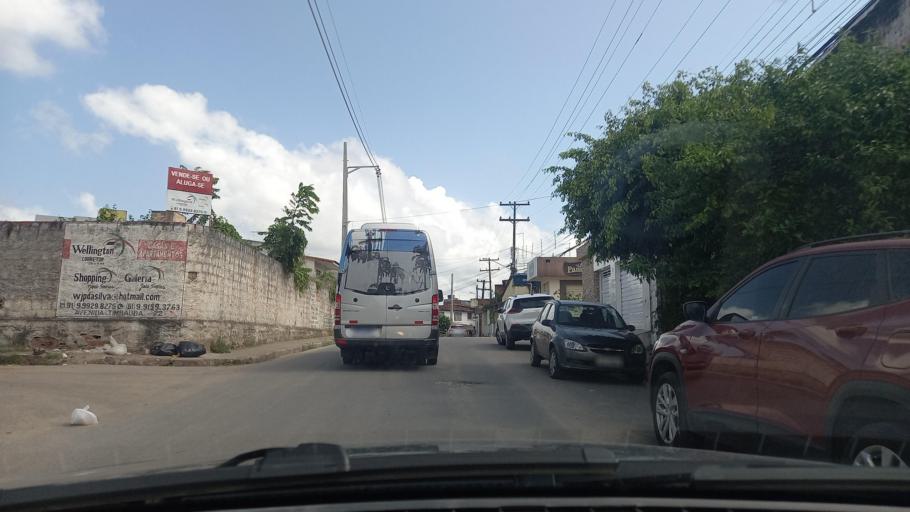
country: BR
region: Pernambuco
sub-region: Goiana
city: Goiana
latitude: -7.5652
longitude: -35.0015
